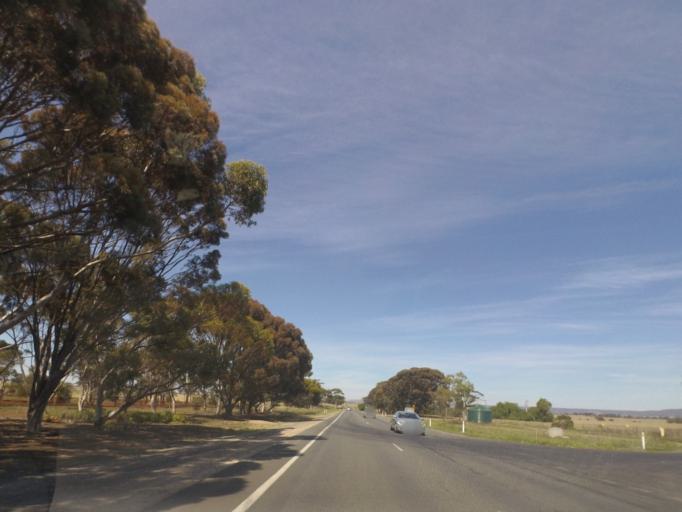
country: AU
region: Victoria
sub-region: Moorabool
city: Bacchus Marsh
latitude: -37.7947
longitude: 144.4142
